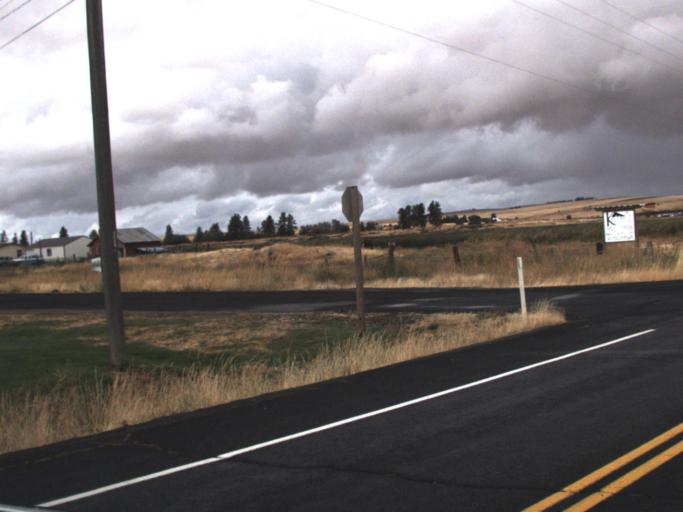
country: US
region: Washington
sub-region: Spokane County
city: Medical Lake
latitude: 47.6733
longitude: -117.8780
